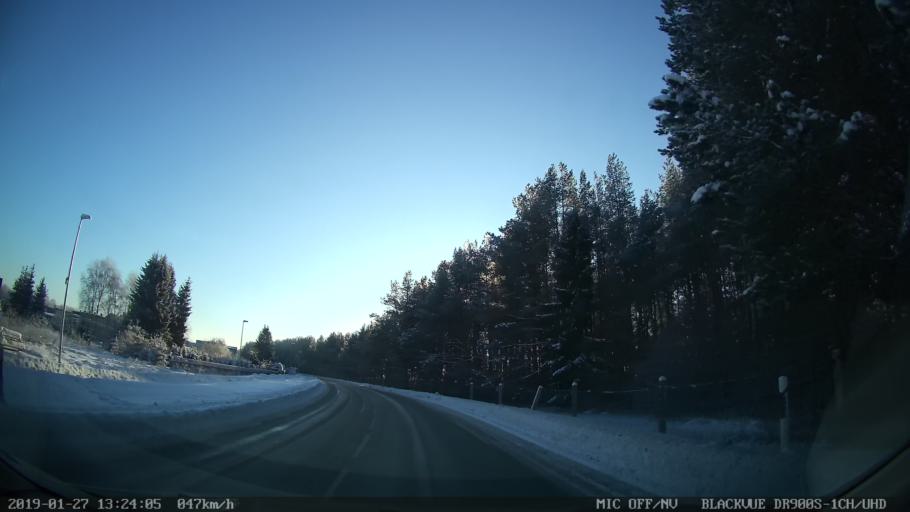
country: EE
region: Harju
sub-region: Tallinna linn
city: Tallinn
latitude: 59.4020
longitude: 24.7902
